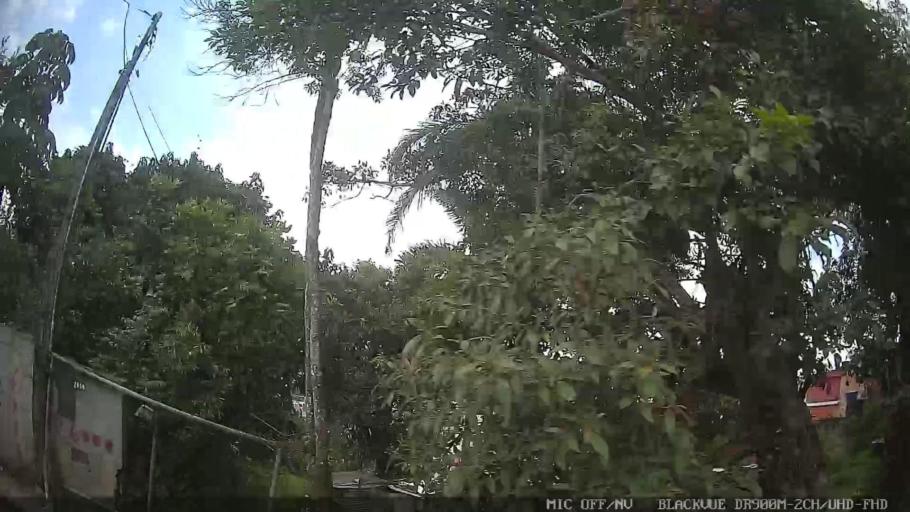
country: BR
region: Sao Paulo
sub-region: Ferraz De Vasconcelos
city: Ferraz de Vasconcelos
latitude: -23.5566
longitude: -46.3665
